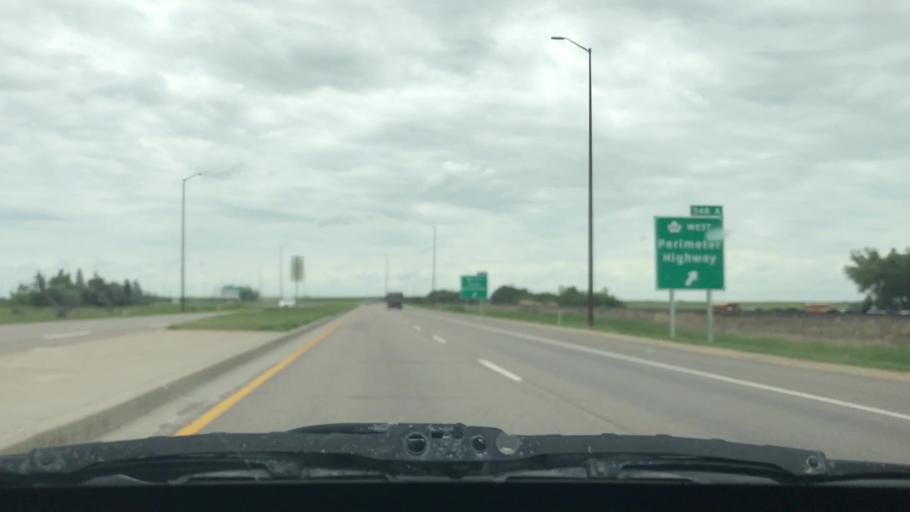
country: CA
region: Manitoba
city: Winnipeg
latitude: 49.8380
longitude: -96.9792
